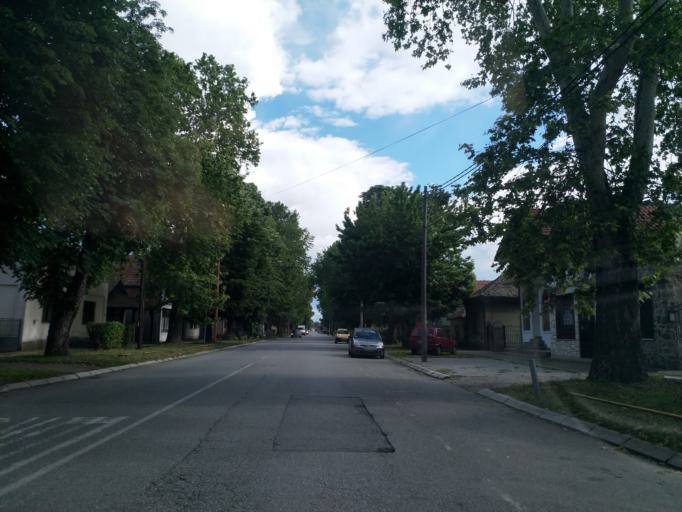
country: RS
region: Central Serbia
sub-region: Pomoravski Okrug
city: Cuprija
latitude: 43.9230
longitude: 21.3735
